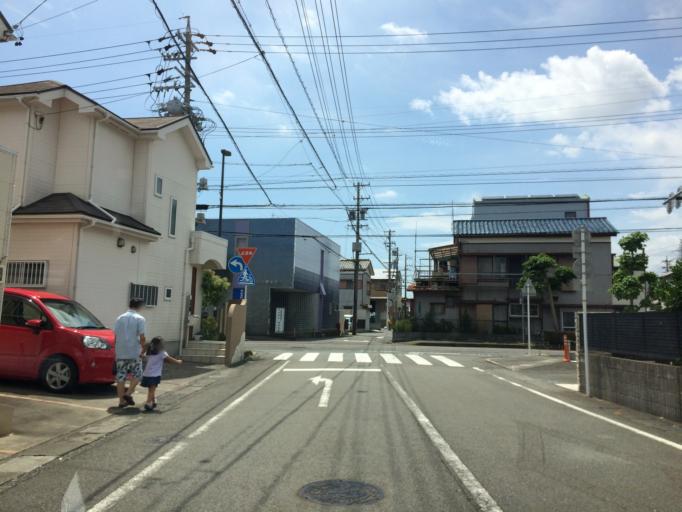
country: JP
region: Shizuoka
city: Yaizu
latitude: 34.8734
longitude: 138.3136
